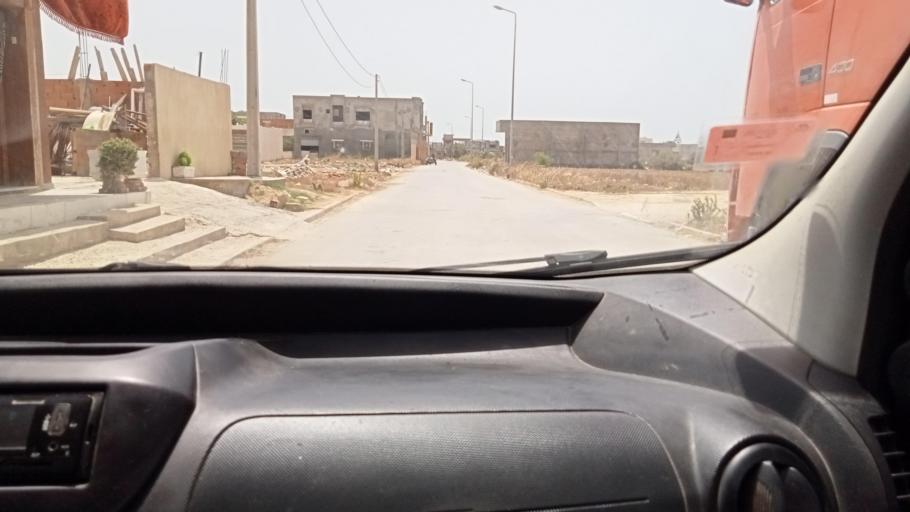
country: TN
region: Nabul
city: Qulaybiyah
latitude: 36.8599
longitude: 11.0847
